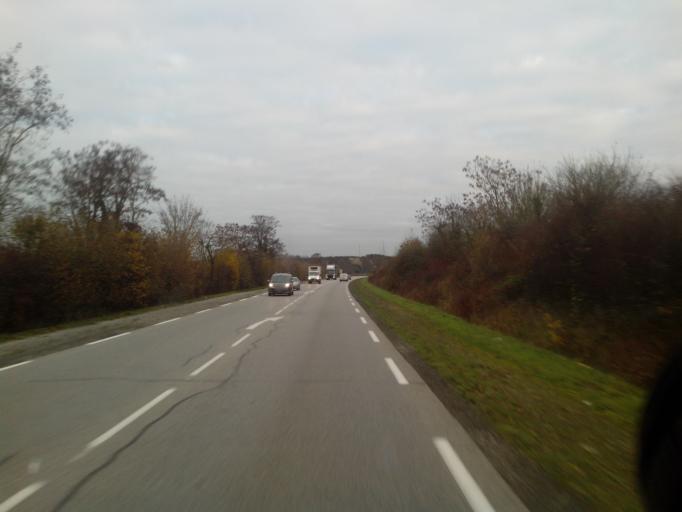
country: FR
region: Poitou-Charentes
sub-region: Departement de la Vienne
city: Migne-Auxances
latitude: 46.6321
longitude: 0.2784
